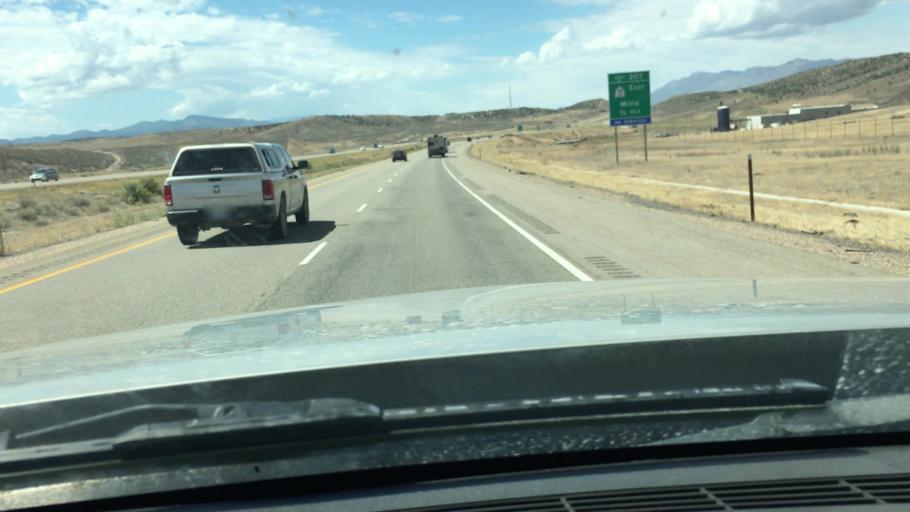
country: US
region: Utah
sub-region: Juab County
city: Nephi
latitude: 39.4929
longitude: -111.9717
